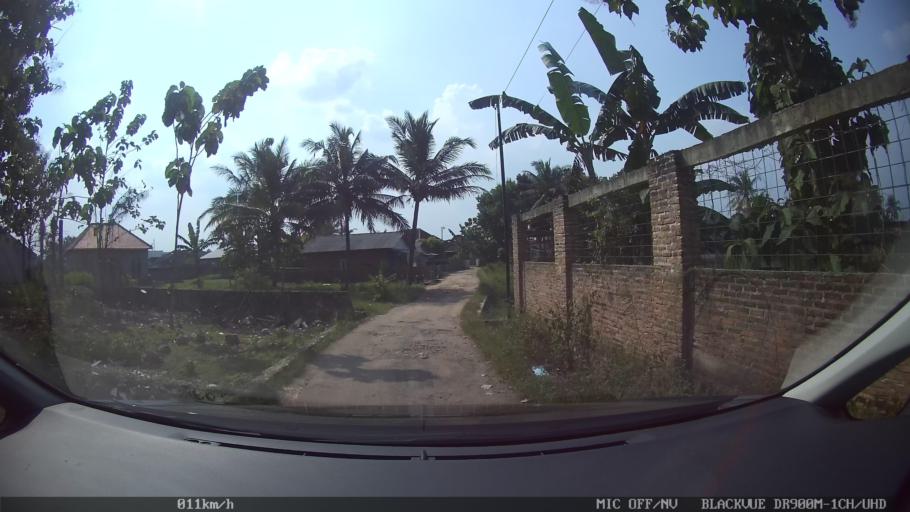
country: ID
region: Lampung
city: Natar
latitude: -5.3131
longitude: 105.2036
